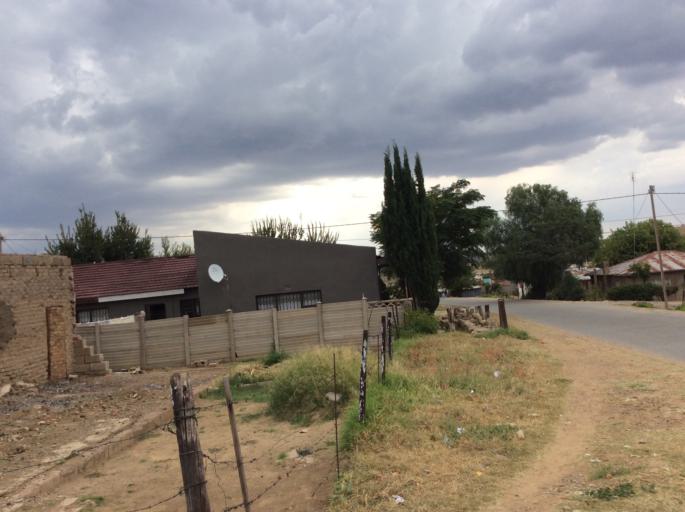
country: LS
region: Mafeteng
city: Mafeteng
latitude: -29.7199
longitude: 27.0314
